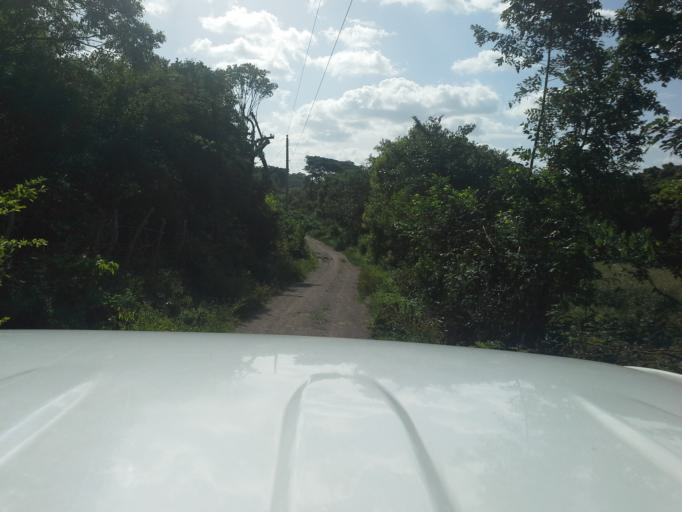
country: NI
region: Matagalpa
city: Ciudad Dario
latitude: 12.6684
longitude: -86.0455
